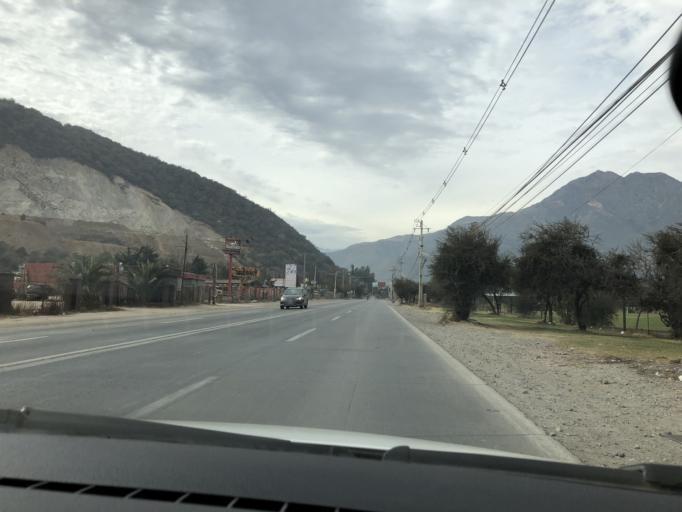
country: CL
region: Santiago Metropolitan
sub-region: Provincia de Cordillera
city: Puente Alto
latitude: -33.5978
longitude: -70.5038
